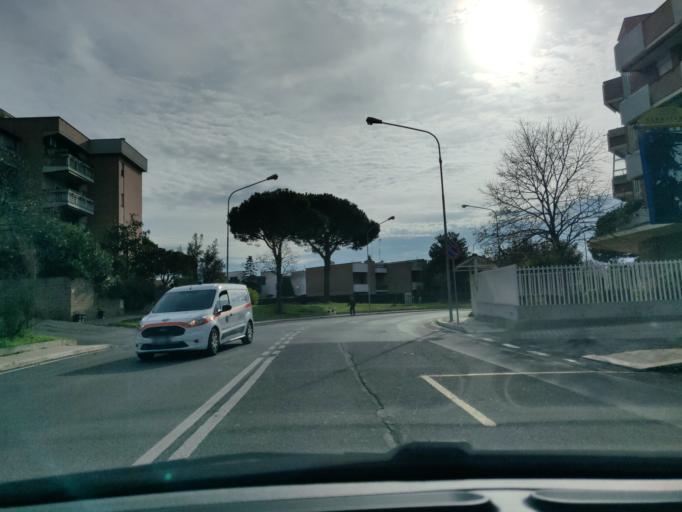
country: IT
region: Latium
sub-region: Citta metropolitana di Roma Capitale
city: Civitavecchia
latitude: 42.1020
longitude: 11.8090
